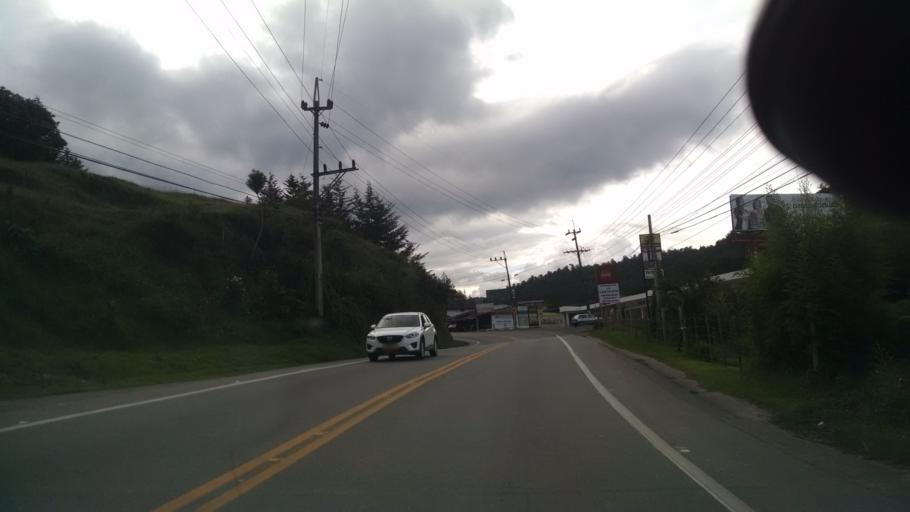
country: CO
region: Antioquia
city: El Retiro
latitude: 6.0913
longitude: -75.4816
